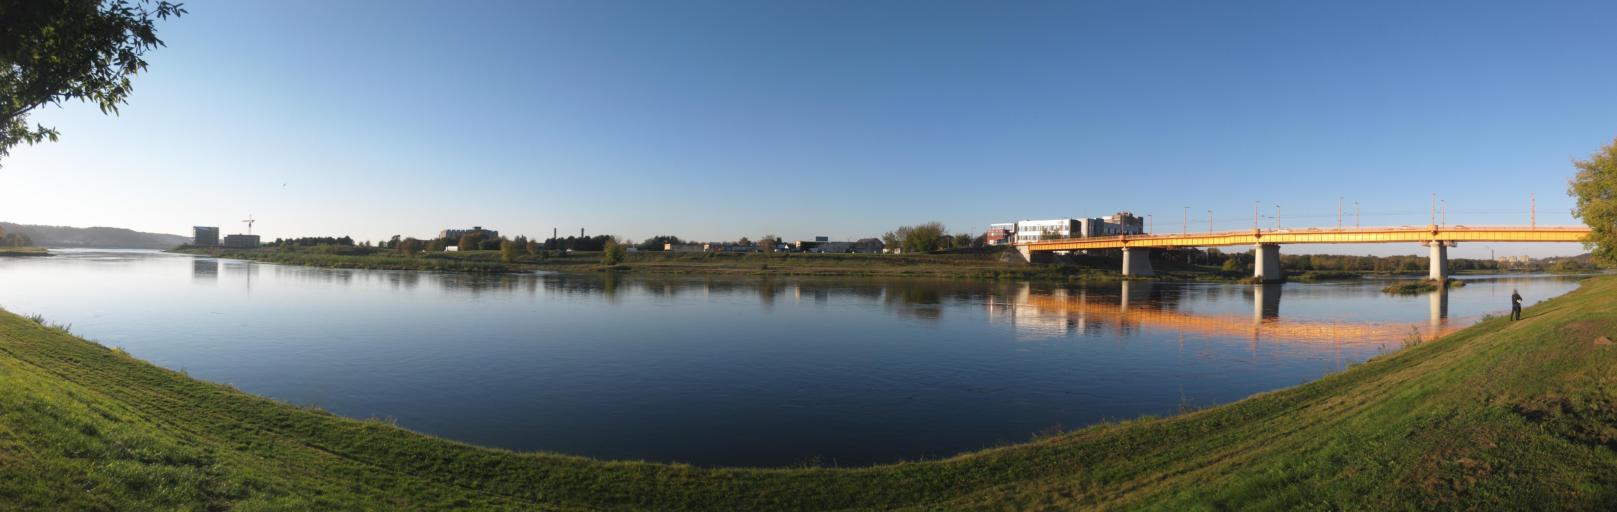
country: LT
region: Kauno apskritis
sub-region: Kaunas
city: Kaunas
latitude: 54.9015
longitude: 23.8906
